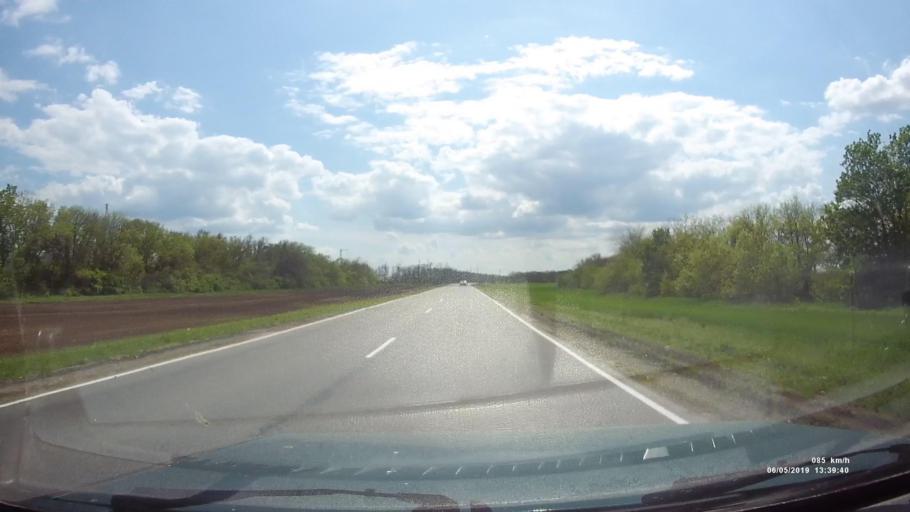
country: RU
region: Rostov
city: Ust'-Donetskiy
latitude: 47.6729
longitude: 40.7010
